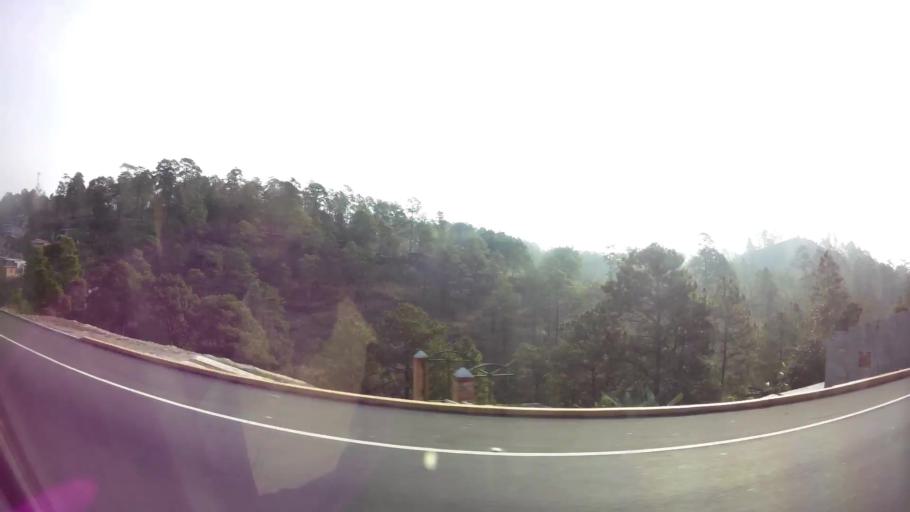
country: HN
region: Francisco Morazan
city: Zambrano
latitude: 14.2706
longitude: -87.4026
